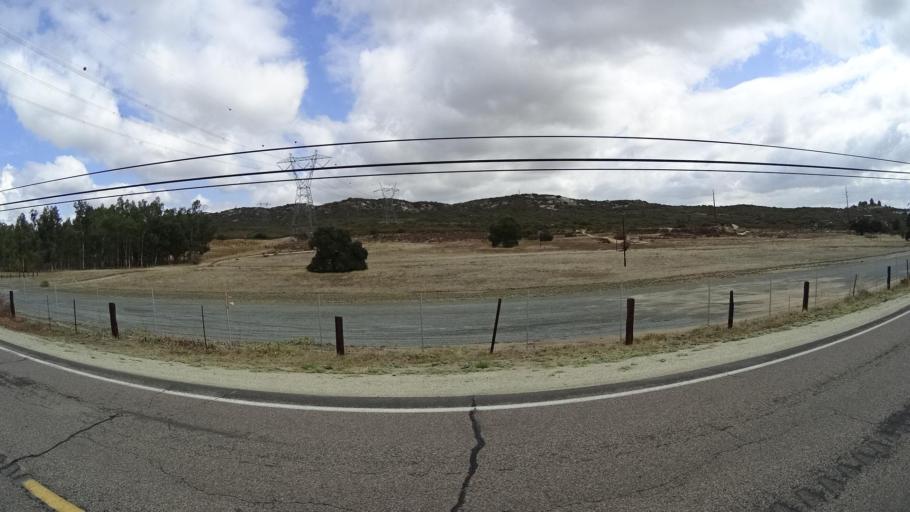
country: US
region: California
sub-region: San Diego County
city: Campo
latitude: 32.6552
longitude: -116.4878
